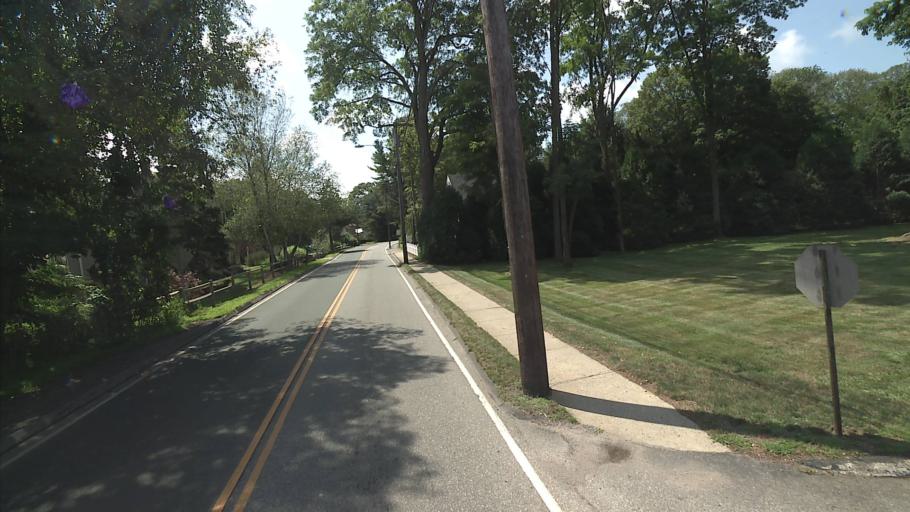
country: US
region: Connecticut
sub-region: Middlesex County
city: Essex Village
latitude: 41.3509
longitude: -72.4169
